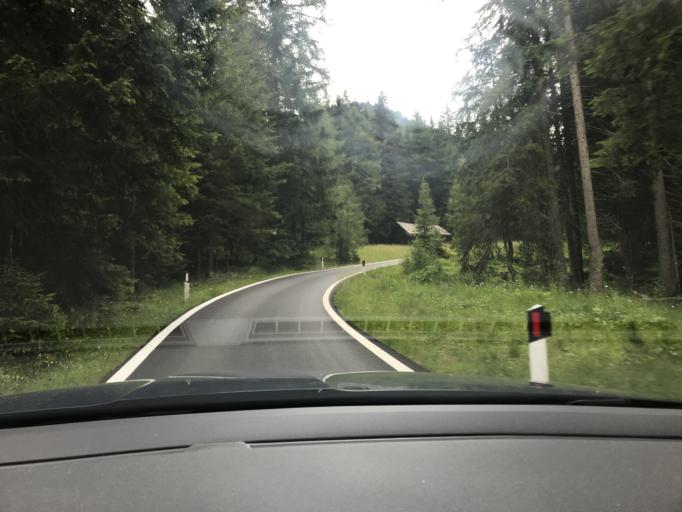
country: IT
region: Trentino-Alto Adige
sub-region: Bolzano
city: San Martino
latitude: 46.8888
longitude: 12.1809
